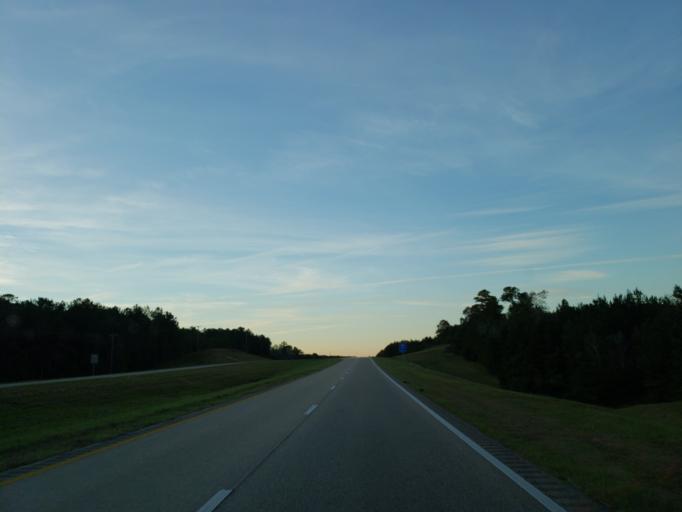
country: US
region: Mississippi
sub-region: Wayne County
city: Belmont
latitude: 31.4790
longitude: -88.4828
